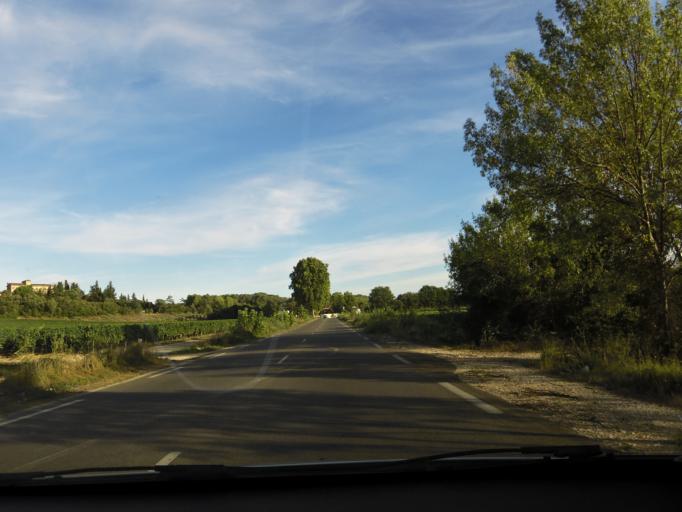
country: FR
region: Languedoc-Roussillon
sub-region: Departement de l'Herault
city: Prades-le-Lez
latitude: 43.6805
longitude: 3.8656
